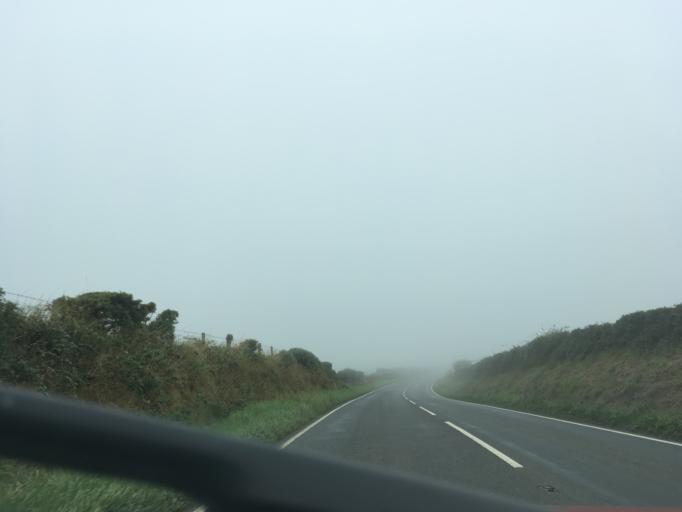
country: GB
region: Wales
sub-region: Pembrokeshire
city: Llanrhian
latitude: 51.8690
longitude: -5.1406
